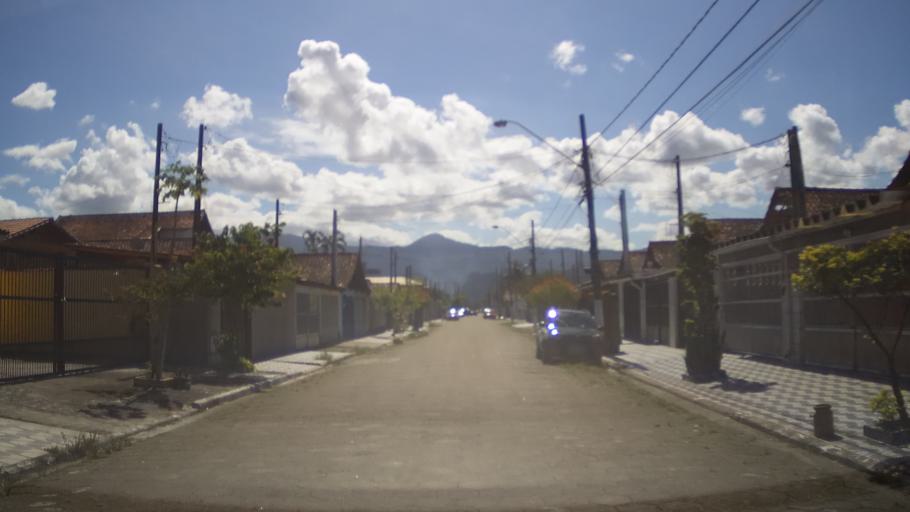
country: BR
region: Sao Paulo
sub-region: Praia Grande
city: Praia Grande
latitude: -24.0355
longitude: -46.4997
